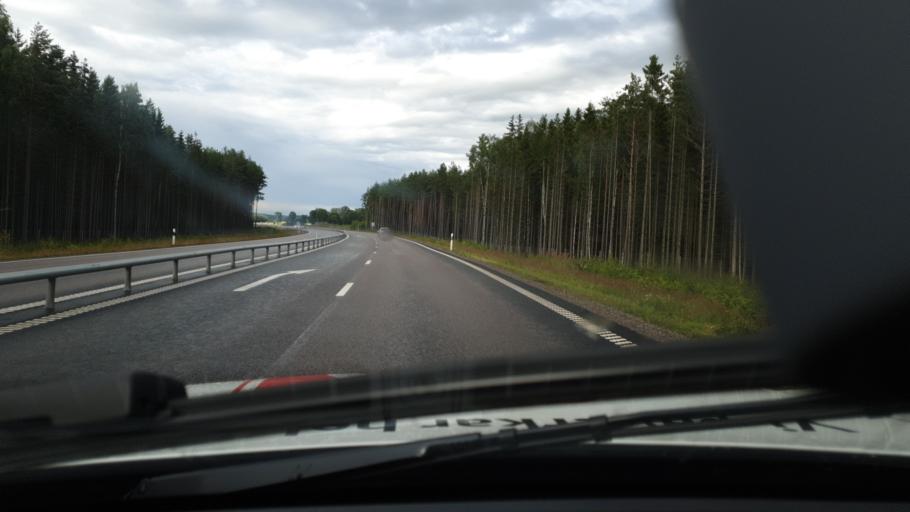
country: SE
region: Vaestra Goetaland
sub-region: Lidkopings Kommun
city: Vinninga
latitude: 58.4795
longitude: 13.2692
